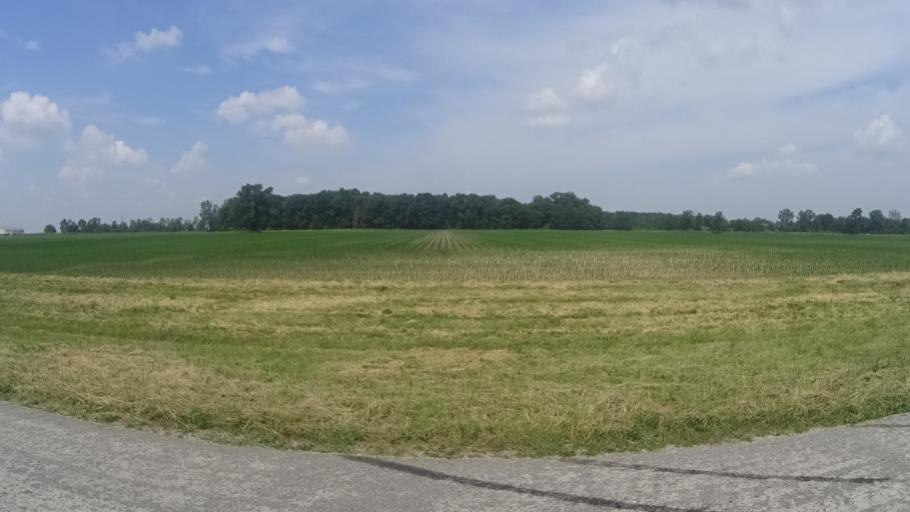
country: US
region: Ohio
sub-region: Erie County
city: Sandusky
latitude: 41.3554
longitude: -82.6943
